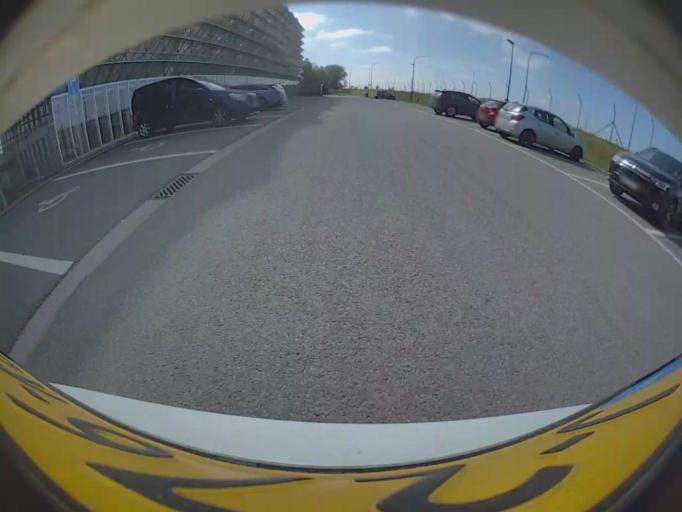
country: BE
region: Wallonia
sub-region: Province du Luxembourg
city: Libin
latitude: 50.0076
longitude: 5.2190
